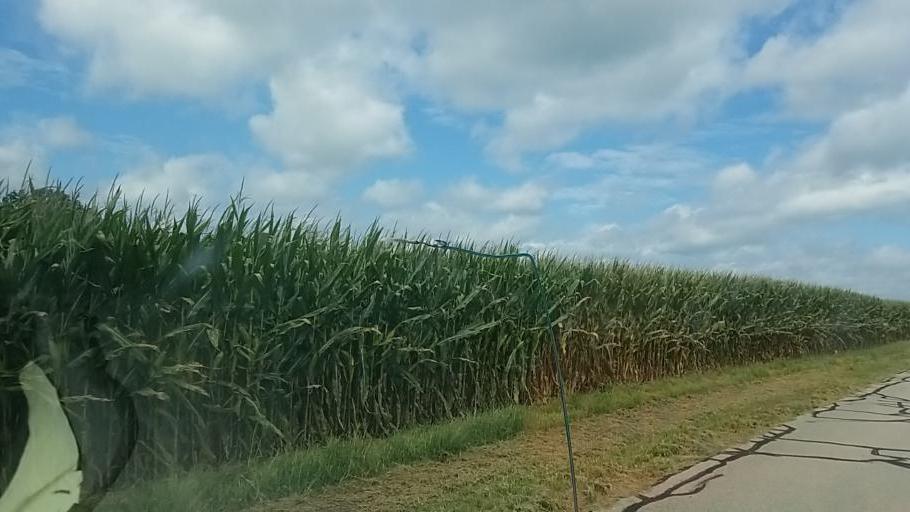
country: US
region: Ohio
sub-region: Fayette County
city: Jeffersonville
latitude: 39.6948
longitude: -83.5764
